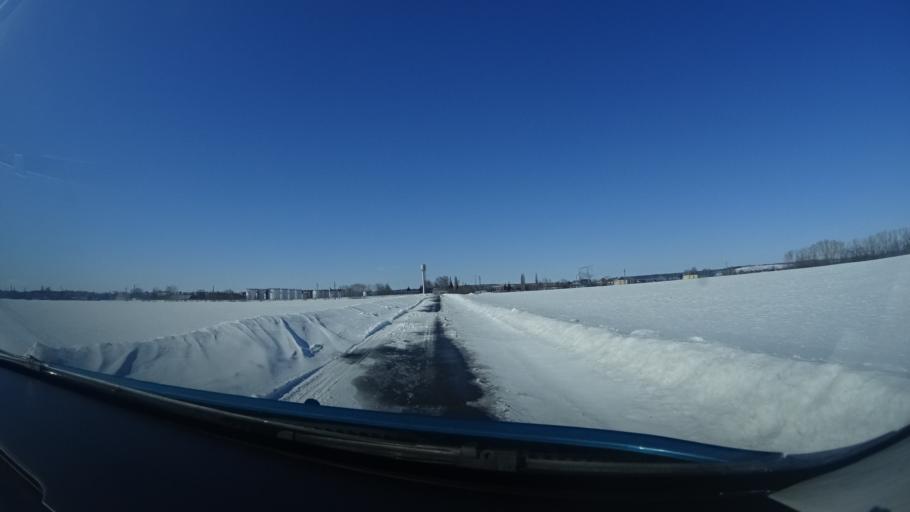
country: RU
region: Bashkortostan
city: Chishmy
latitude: 54.5856
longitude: 55.4117
